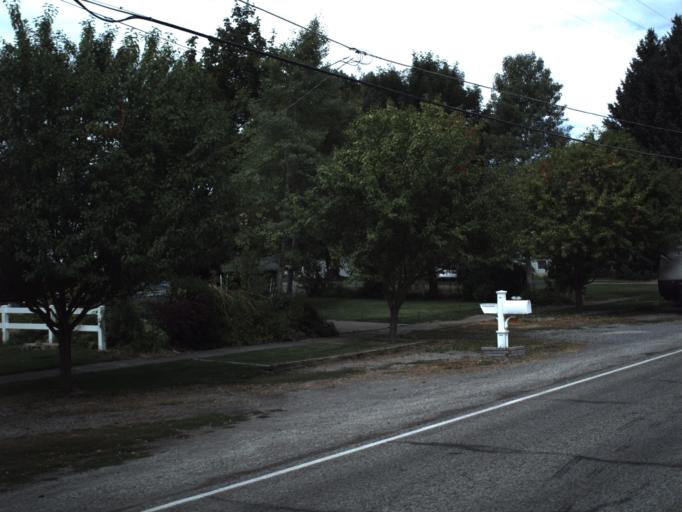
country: US
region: Utah
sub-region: Cache County
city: Wellsville
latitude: 41.6332
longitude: -111.9345
